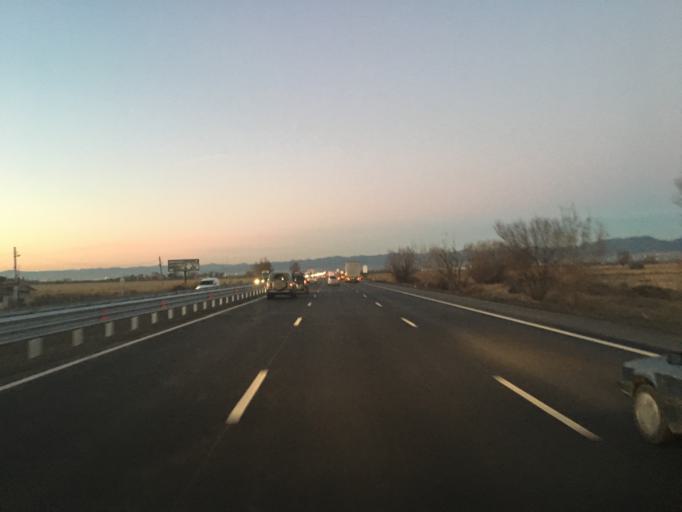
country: BG
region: Sofia-Capital
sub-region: Stolichna Obshtina
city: Sofia
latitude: 42.6882
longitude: 23.4532
